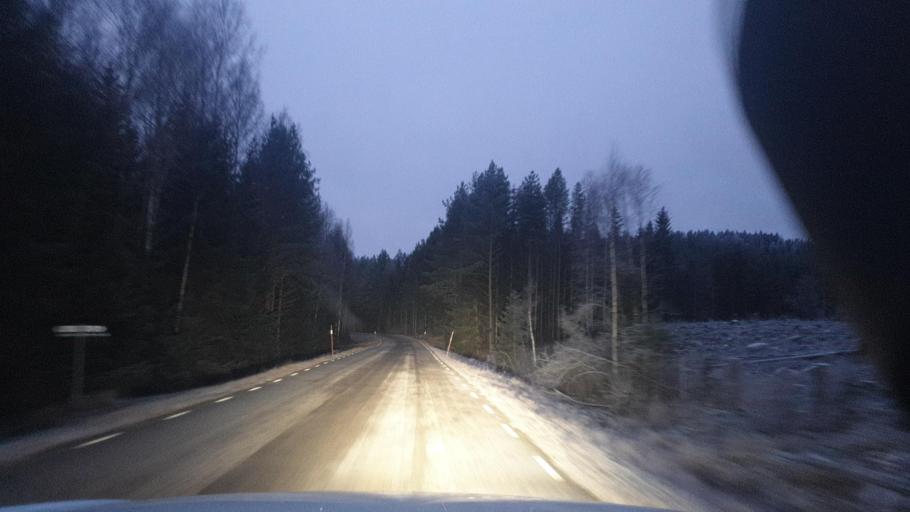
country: SE
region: Vaermland
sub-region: Arvika Kommun
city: Arvika
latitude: 59.5439
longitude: 12.3992
